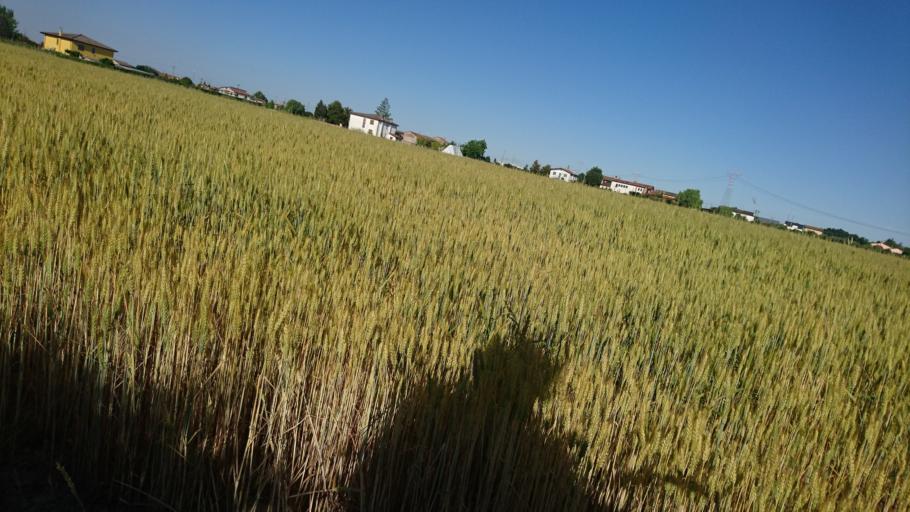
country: IT
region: Veneto
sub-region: Provincia di Padova
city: Ponte San Nicolo
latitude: 45.3570
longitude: 11.9118
